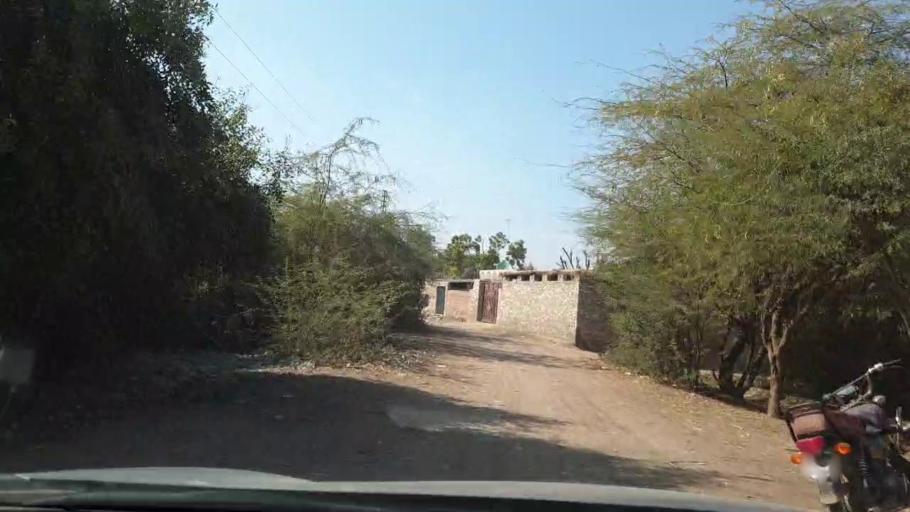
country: PK
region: Sindh
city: Berani
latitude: 25.6894
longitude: 68.7792
